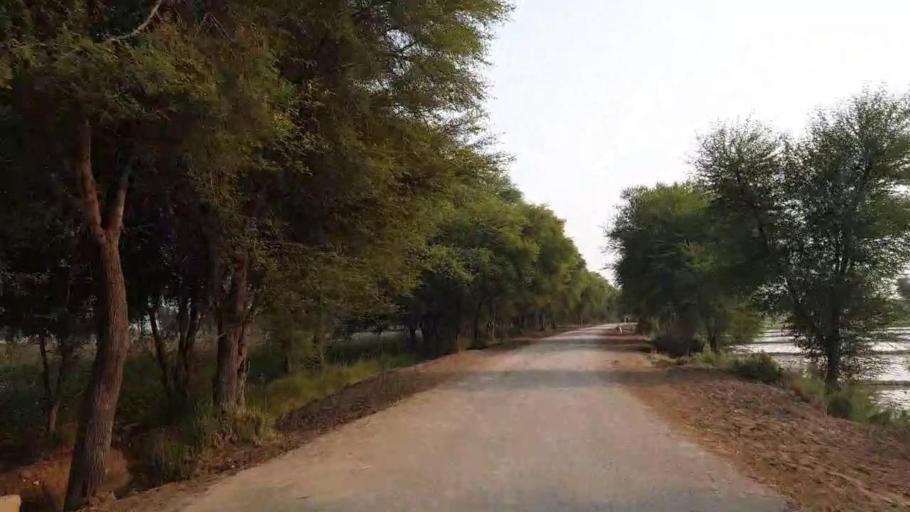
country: PK
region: Sindh
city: Bhan
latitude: 26.5028
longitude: 67.7600
